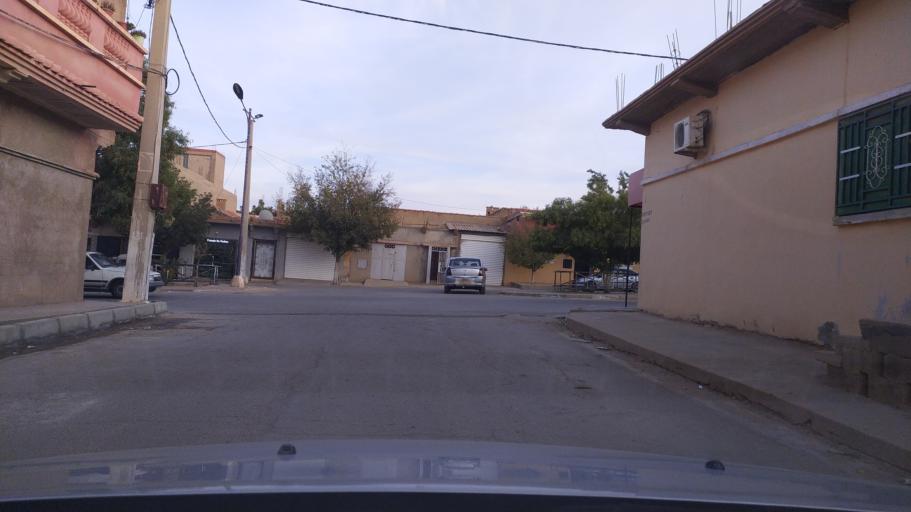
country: DZ
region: Tiaret
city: Frenda
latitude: 34.8988
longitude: 1.2367
